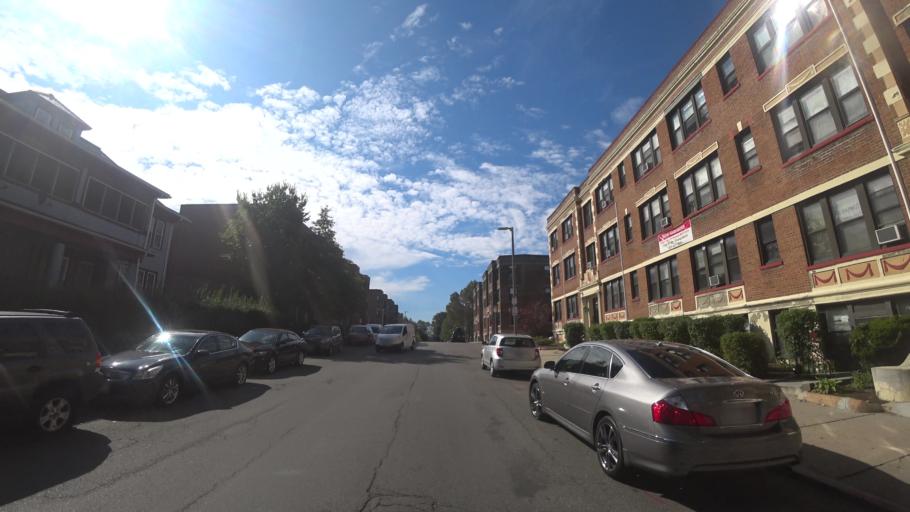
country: US
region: Massachusetts
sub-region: Suffolk County
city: Jamaica Plain
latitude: 42.3096
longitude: -71.0876
